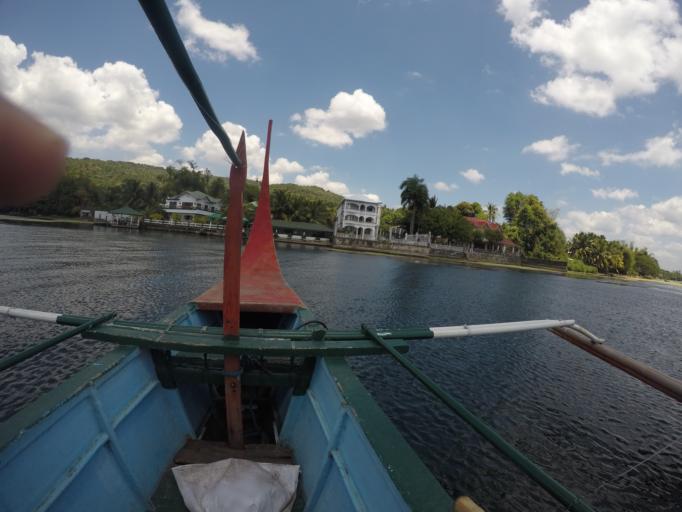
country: PH
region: Calabarzon
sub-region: Province of Batangas
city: Sampaloc
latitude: 14.0824
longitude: 120.9890
